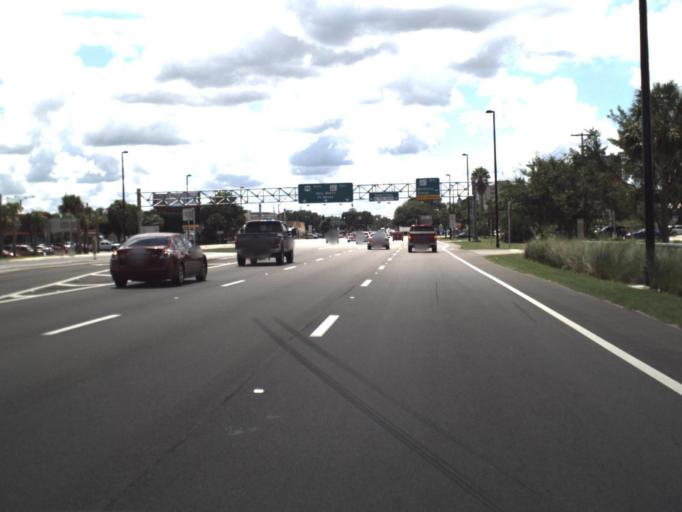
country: US
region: Florida
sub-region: Polk County
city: Bartow
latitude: 27.9068
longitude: -81.8436
